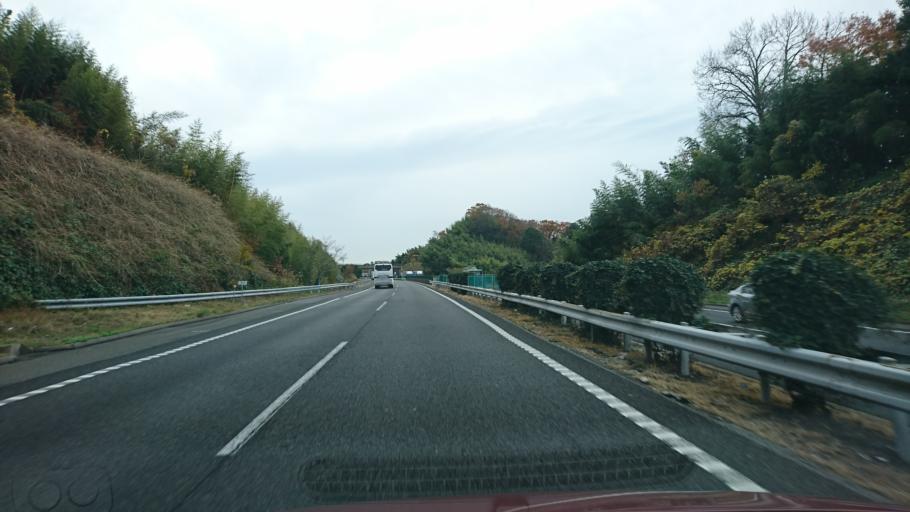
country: JP
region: Hyogo
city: Sandacho
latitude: 34.8212
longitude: 135.1332
